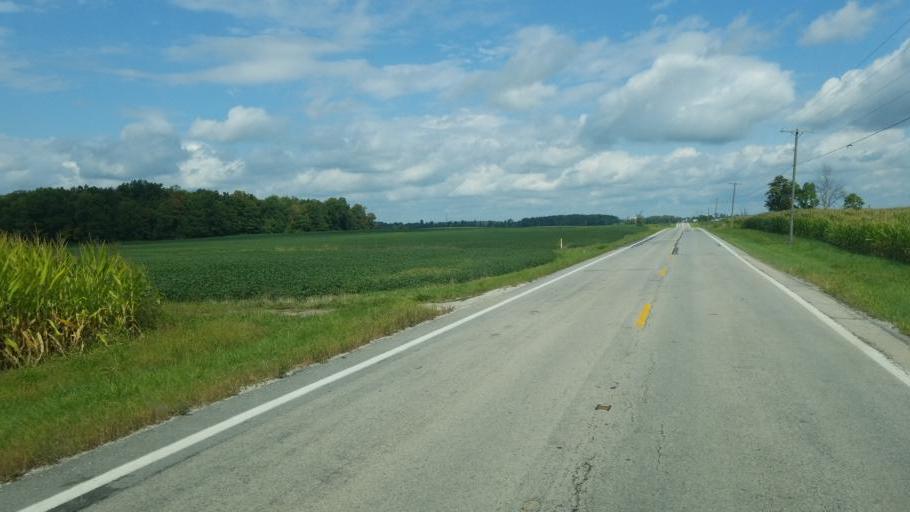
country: US
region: Ohio
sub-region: Seneca County
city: Tiffin
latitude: 41.0864
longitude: -83.0152
